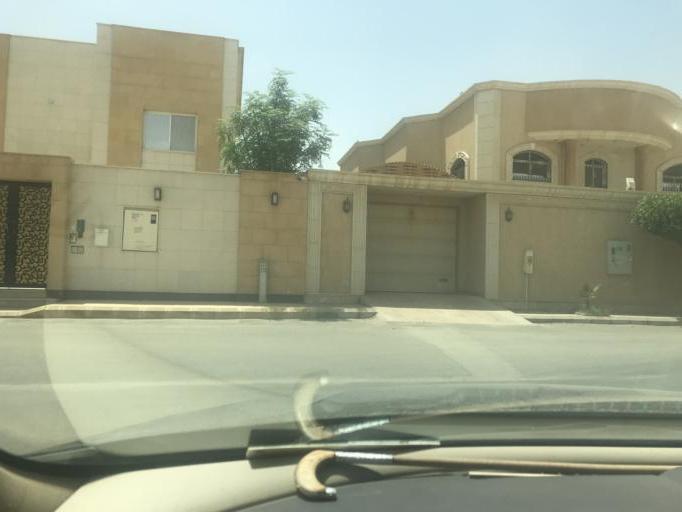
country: SA
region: Ar Riyad
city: Riyadh
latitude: 24.7977
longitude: 46.6969
